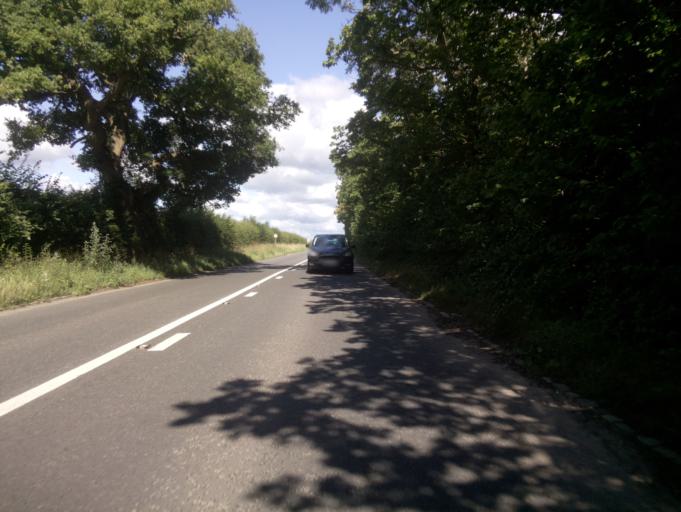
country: GB
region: England
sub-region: Gloucestershire
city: Newent
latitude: 51.9216
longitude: -2.3694
